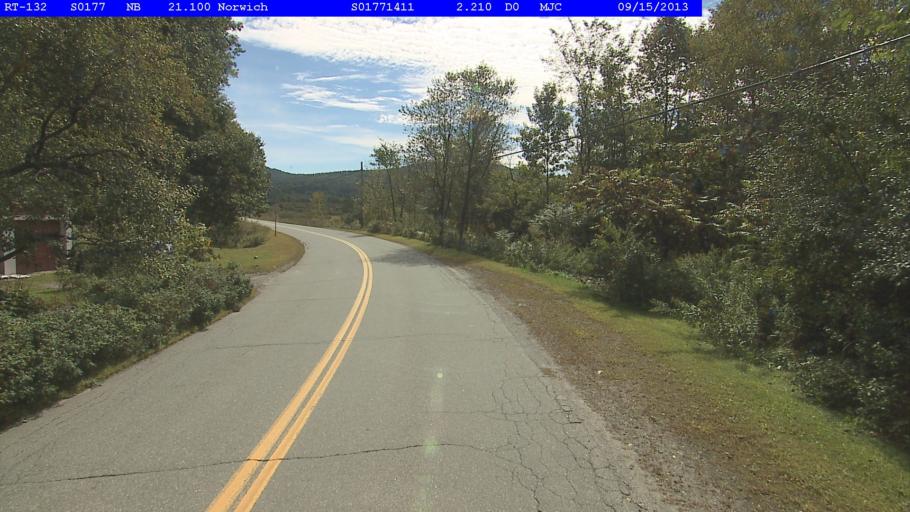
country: US
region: New Hampshire
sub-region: Grafton County
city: Hanover
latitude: 43.7624
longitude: -72.2381
